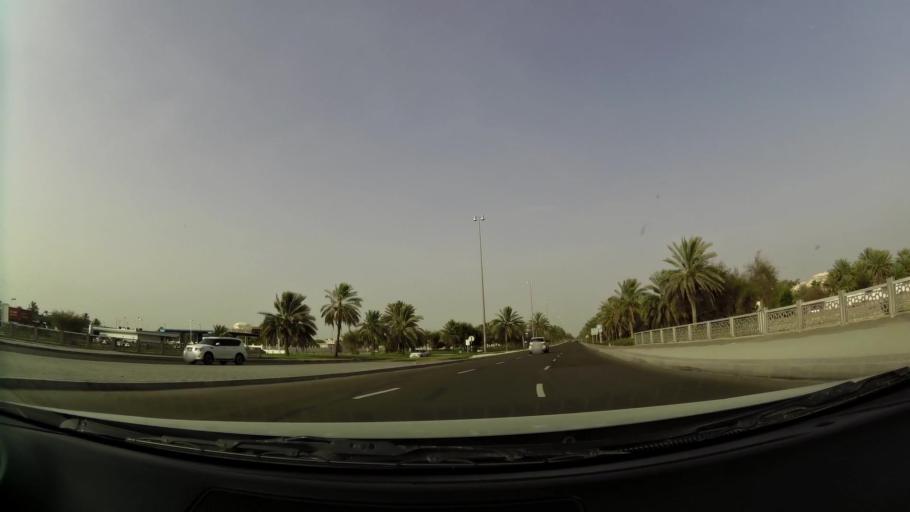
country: AE
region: Abu Dhabi
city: Al Ain
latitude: 24.2171
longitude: 55.6841
